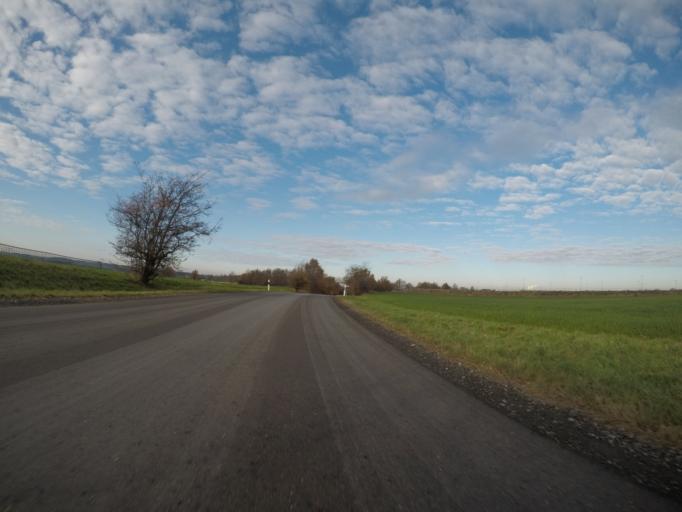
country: DE
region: Thuringia
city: Vollmershain
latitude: 50.8588
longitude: 12.3043
